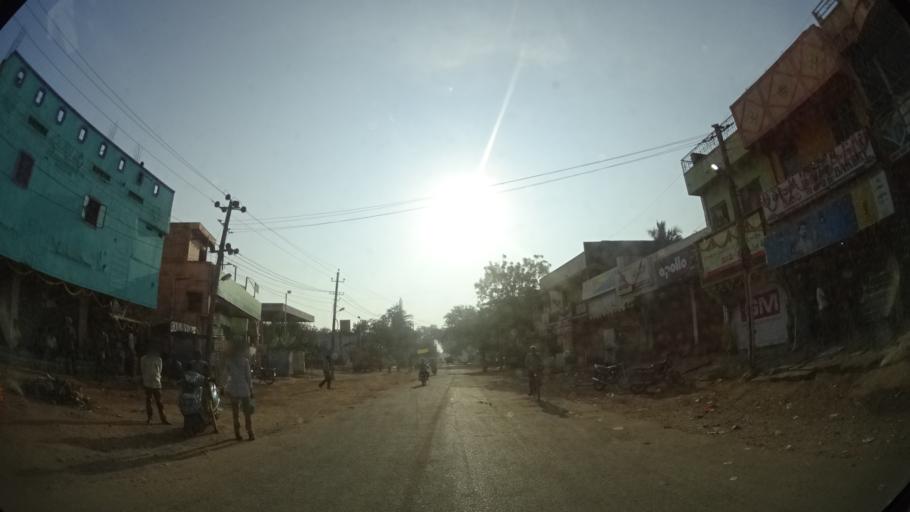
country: IN
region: Karnataka
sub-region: Bellary
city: Hospet
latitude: 15.2662
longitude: 76.3992
